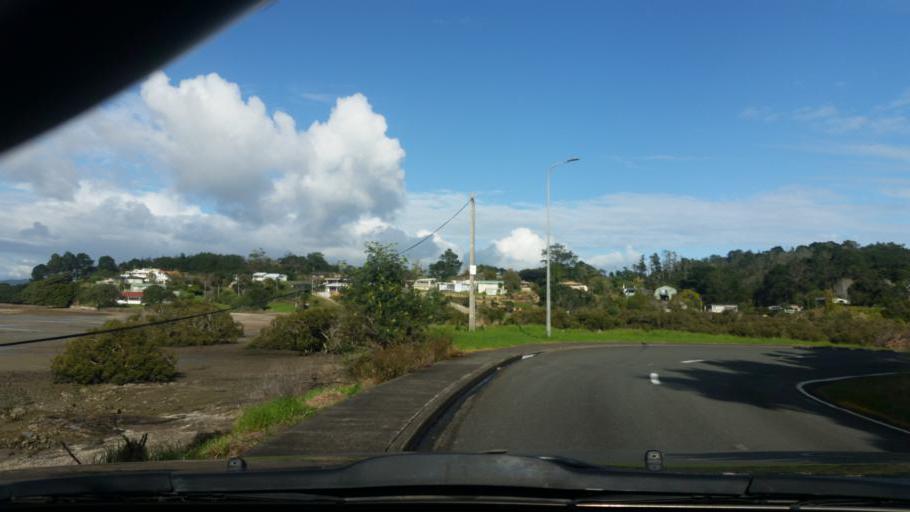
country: NZ
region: Auckland
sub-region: Auckland
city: Wellsford
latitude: -36.2525
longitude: 174.2477
